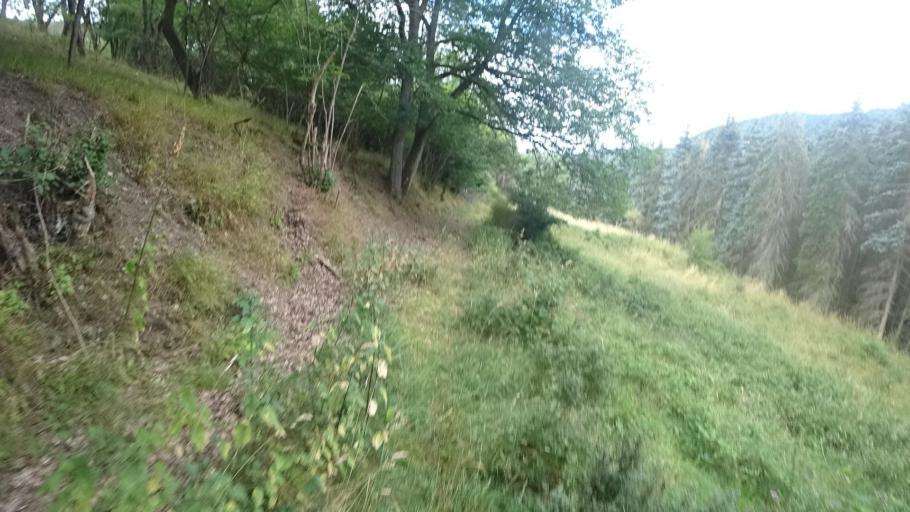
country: DE
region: Rheinland-Pfalz
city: Heckenbach
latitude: 50.4795
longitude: 7.0372
